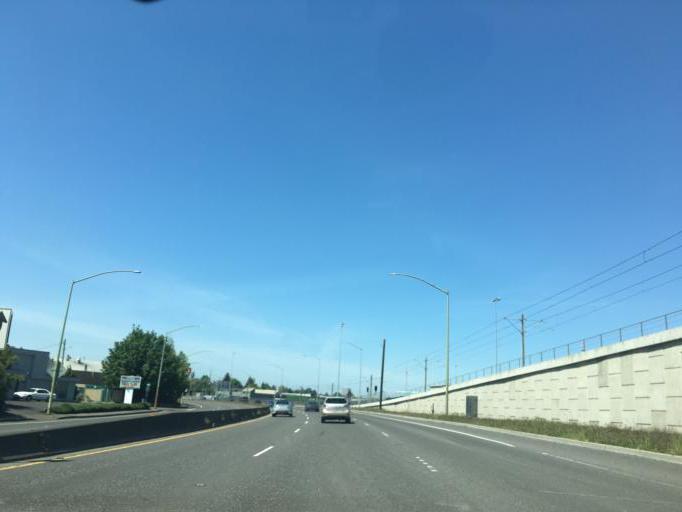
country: US
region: Oregon
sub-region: Clackamas County
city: Milwaukie
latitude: 45.4833
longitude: -122.6434
